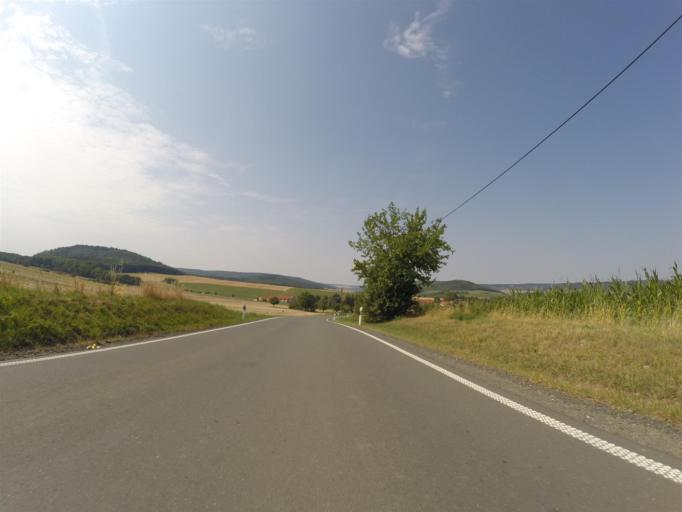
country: DE
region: Thuringia
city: Nausnitz
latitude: 50.9313
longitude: 11.7196
